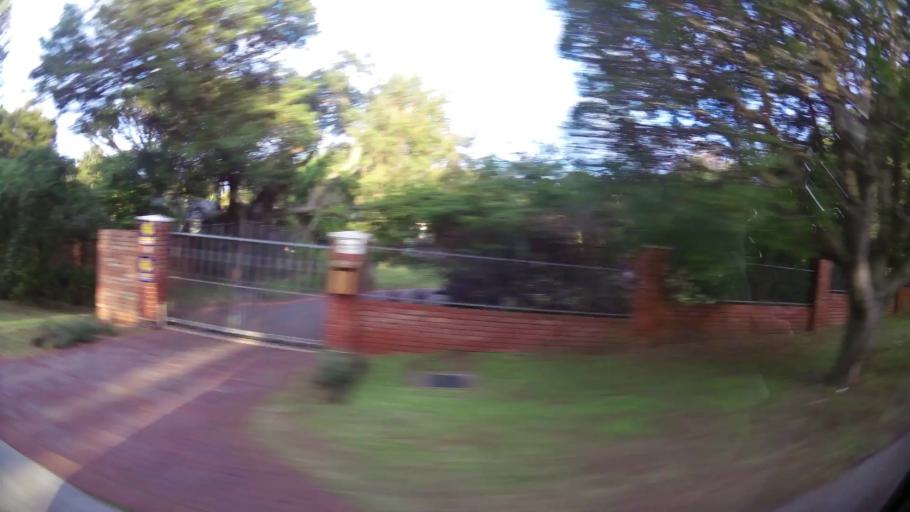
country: ZA
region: Eastern Cape
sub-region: Nelson Mandela Bay Metropolitan Municipality
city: Port Elizabeth
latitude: -33.9784
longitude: 25.5788
